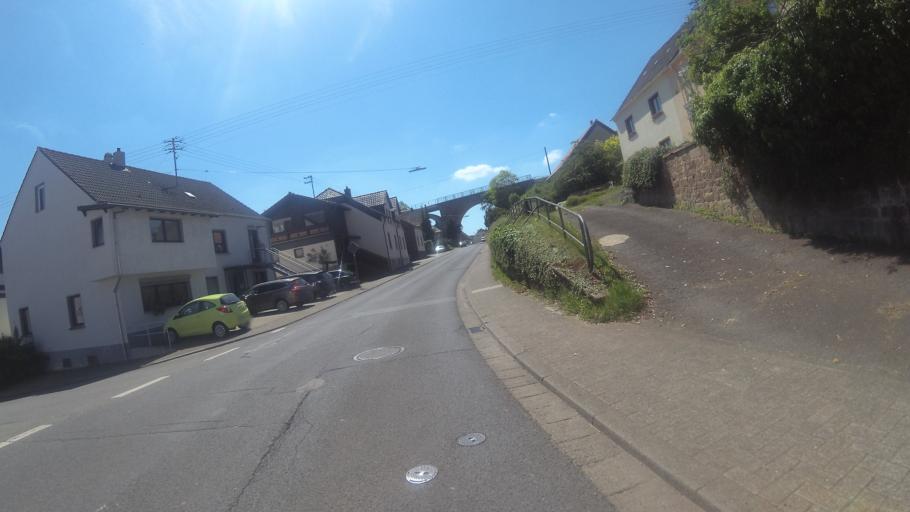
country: DE
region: Saarland
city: Heusweiler
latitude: 49.3605
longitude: 6.9358
